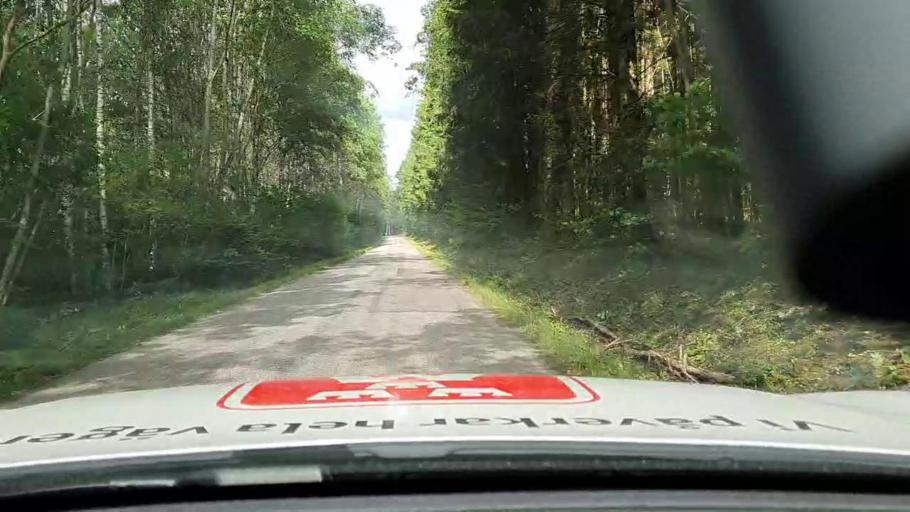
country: SE
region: Vaestra Goetaland
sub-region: Karlsborgs Kommun
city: Molltorp
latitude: 58.5782
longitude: 14.2677
